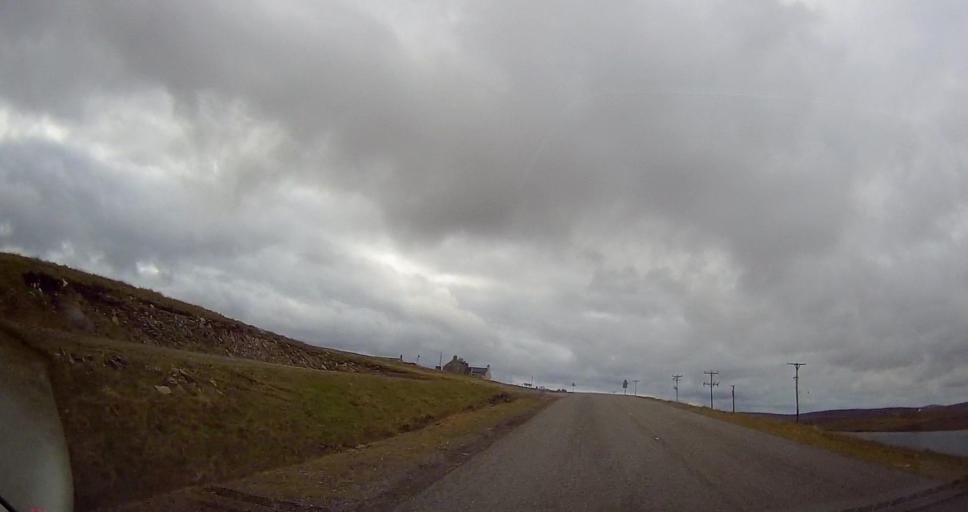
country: GB
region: Scotland
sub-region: Shetland Islands
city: Shetland
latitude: 60.6689
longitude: -1.0619
